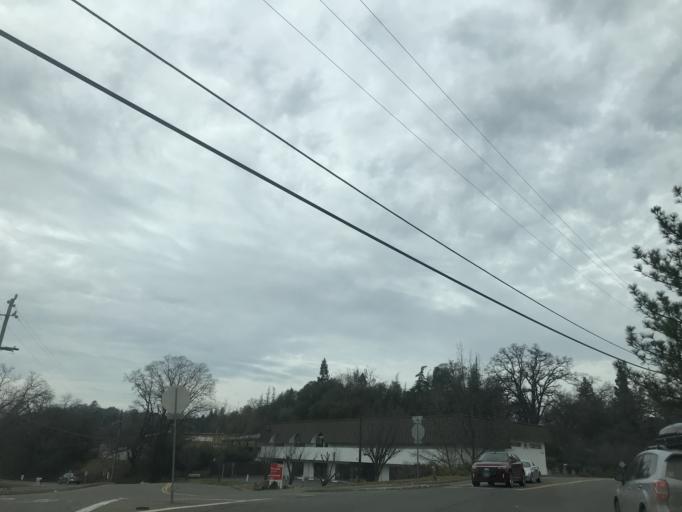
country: US
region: California
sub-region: El Dorado County
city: Placerville
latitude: 38.7346
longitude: -120.8278
